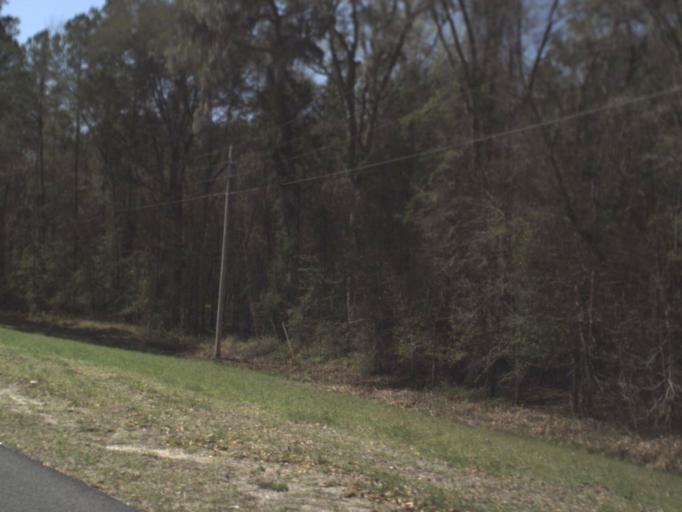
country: US
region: Florida
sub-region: Jefferson County
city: Monticello
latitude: 30.4766
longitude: -84.0226
